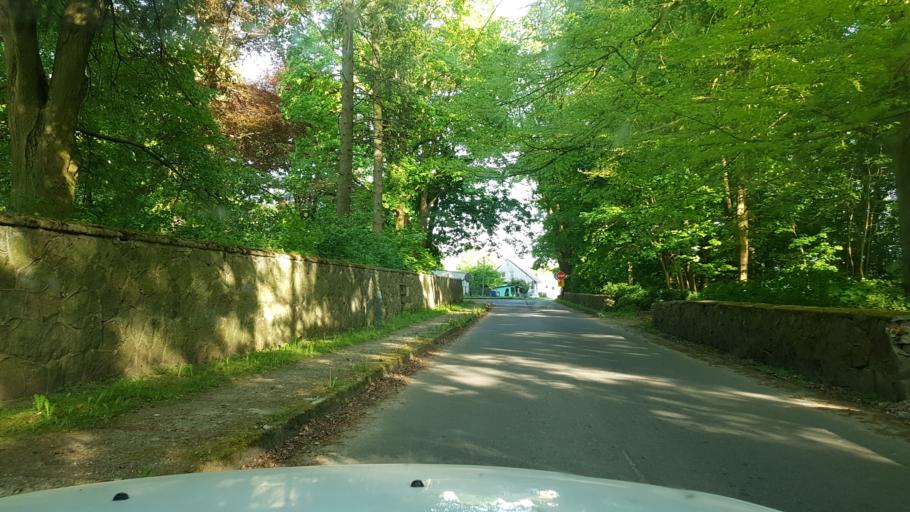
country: PL
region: West Pomeranian Voivodeship
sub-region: Powiat lobeski
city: Radowo Male
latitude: 53.6493
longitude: 15.3687
